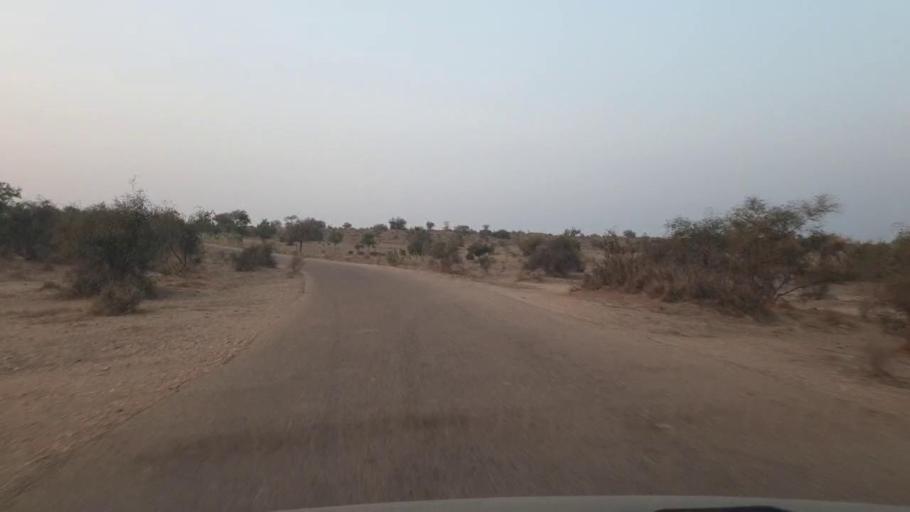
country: PK
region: Sindh
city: Umarkot
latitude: 25.3354
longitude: 70.0578
